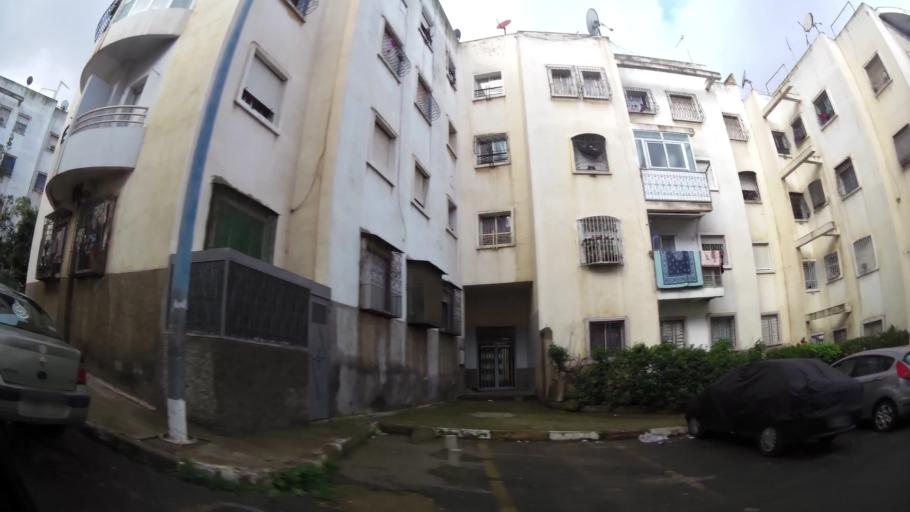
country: MA
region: Grand Casablanca
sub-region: Mediouna
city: Tit Mellil
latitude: 33.5818
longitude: -7.5224
